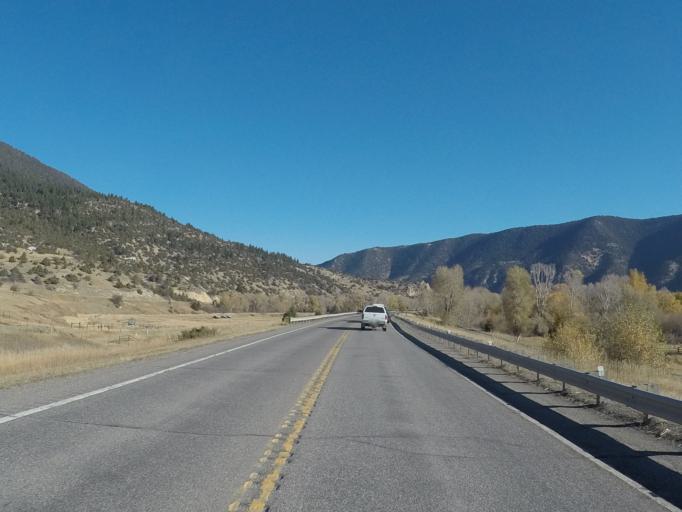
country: US
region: Montana
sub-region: Park County
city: Livingston
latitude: 45.5735
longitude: -110.5875
